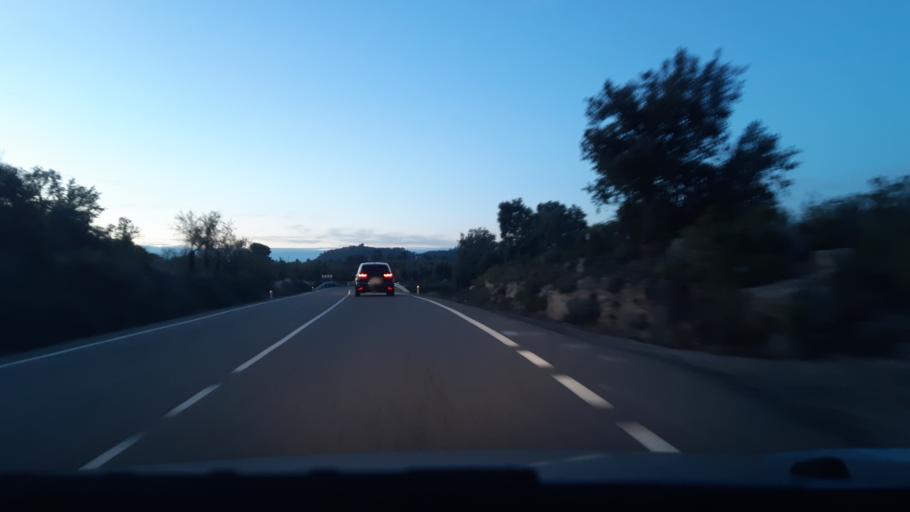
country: ES
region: Aragon
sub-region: Provincia de Teruel
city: Calaceite
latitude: 40.9912
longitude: 0.1982
